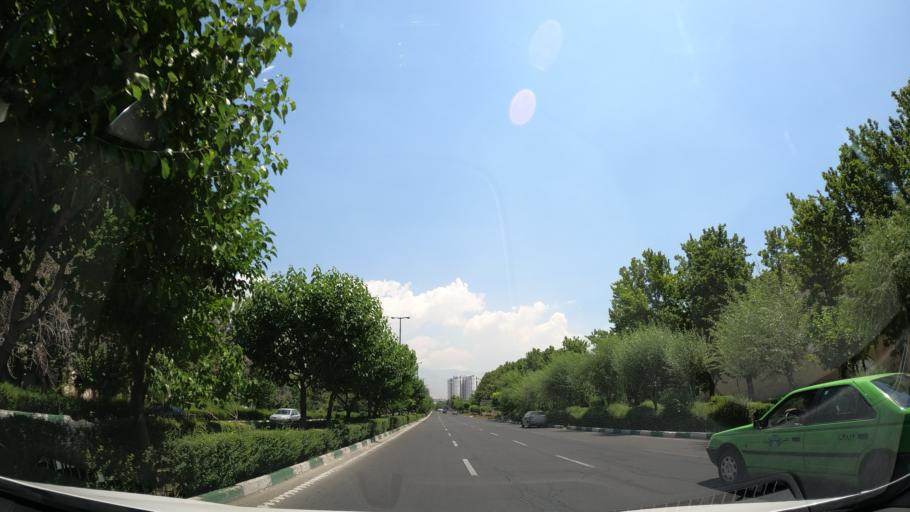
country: IR
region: Tehran
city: Tajrish
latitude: 35.7591
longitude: 51.3742
